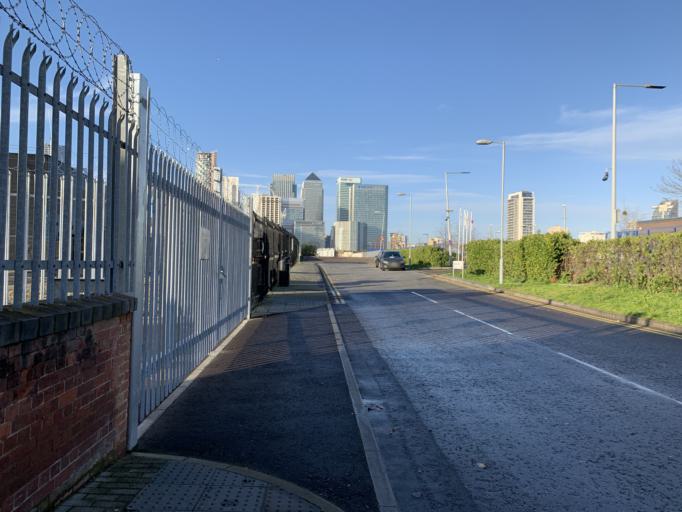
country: GB
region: England
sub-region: Greater London
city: Poplar
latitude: 51.5017
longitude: 0.0000
